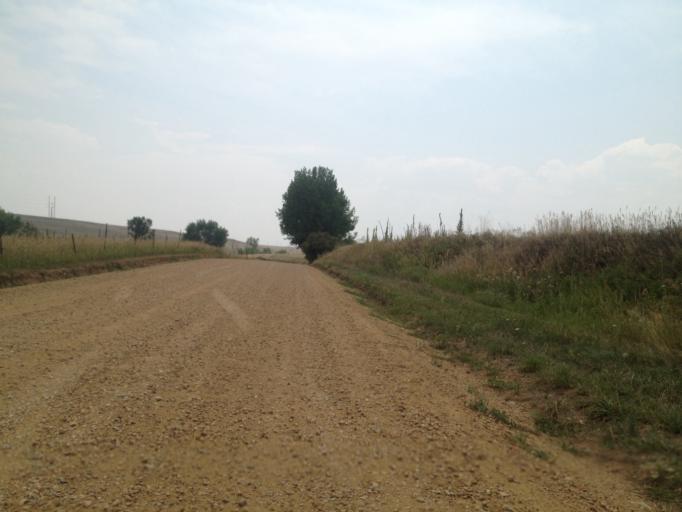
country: US
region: Colorado
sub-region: Boulder County
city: Superior
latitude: 39.9495
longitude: -105.1843
